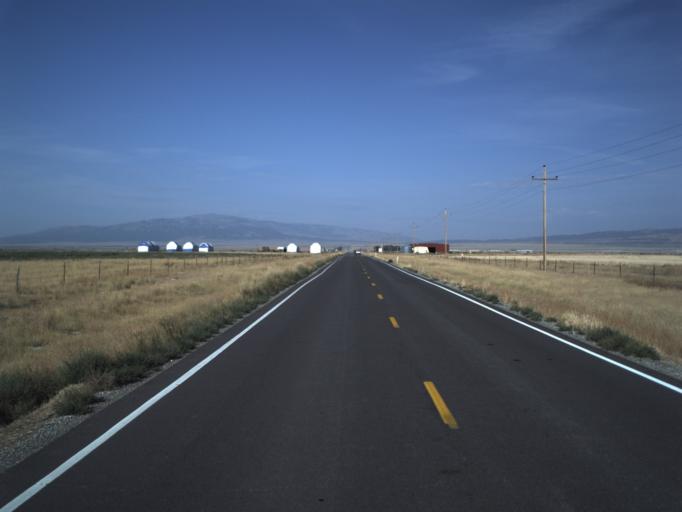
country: US
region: Idaho
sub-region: Oneida County
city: Malad City
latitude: 41.9671
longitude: -112.8646
